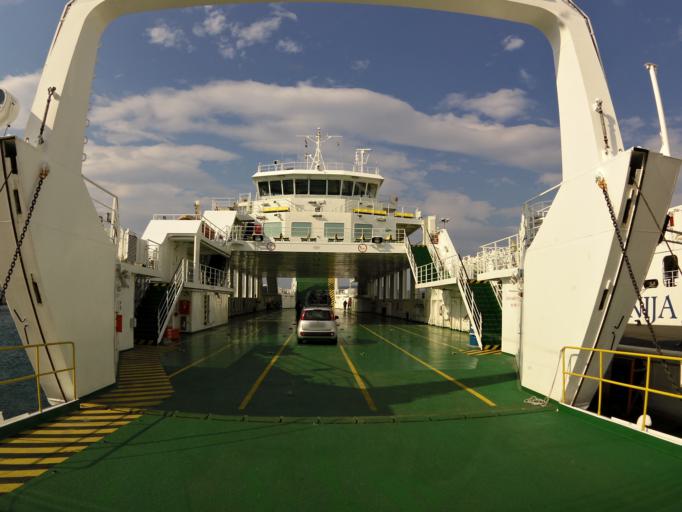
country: HR
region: Zadarska
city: Zadar
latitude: 44.0942
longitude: 15.2558
